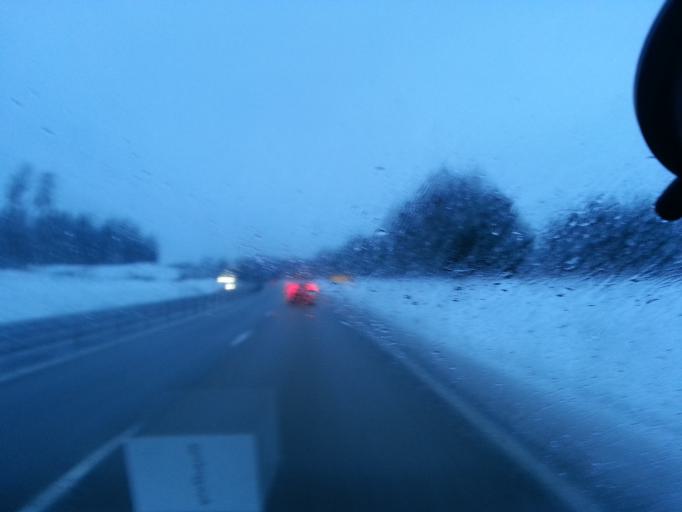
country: SE
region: Kronoberg
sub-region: Ljungby Kommun
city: Lagan
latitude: 56.9714
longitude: 14.0177
